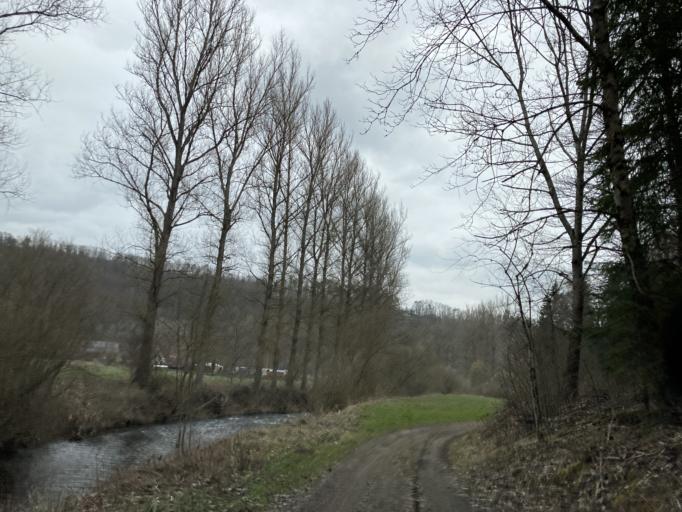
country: DE
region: Baden-Wuerttemberg
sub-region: Tuebingen Region
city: Hirrlingen
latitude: 48.4238
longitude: 8.8663
